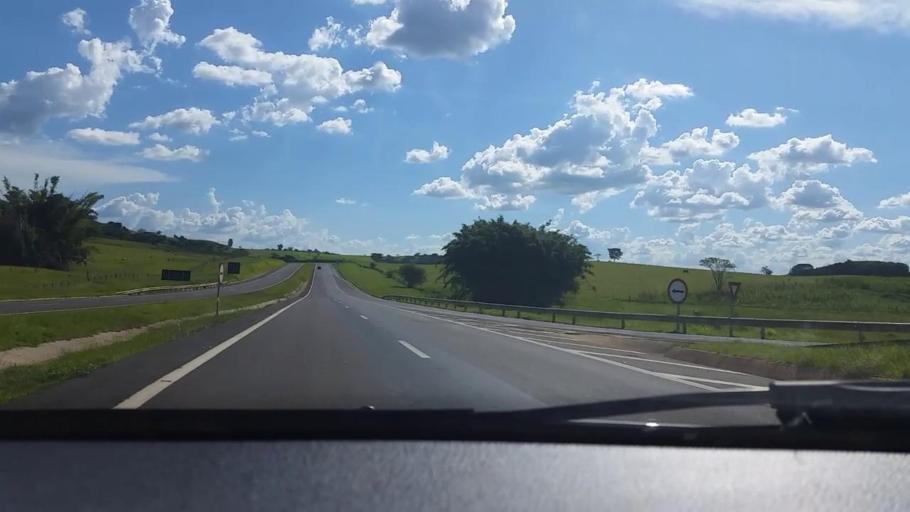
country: BR
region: Sao Paulo
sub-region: Bauru
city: Bauru
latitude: -22.4250
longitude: -49.1261
